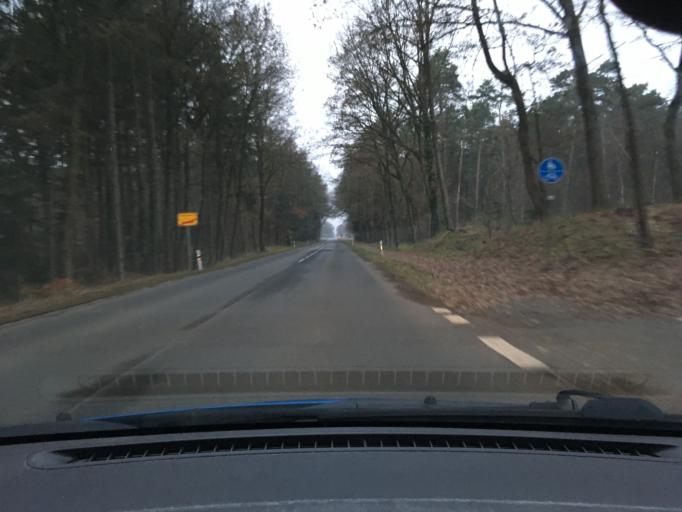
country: DE
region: Lower Saxony
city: Bispingen
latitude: 53.1176
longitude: 9.9538
